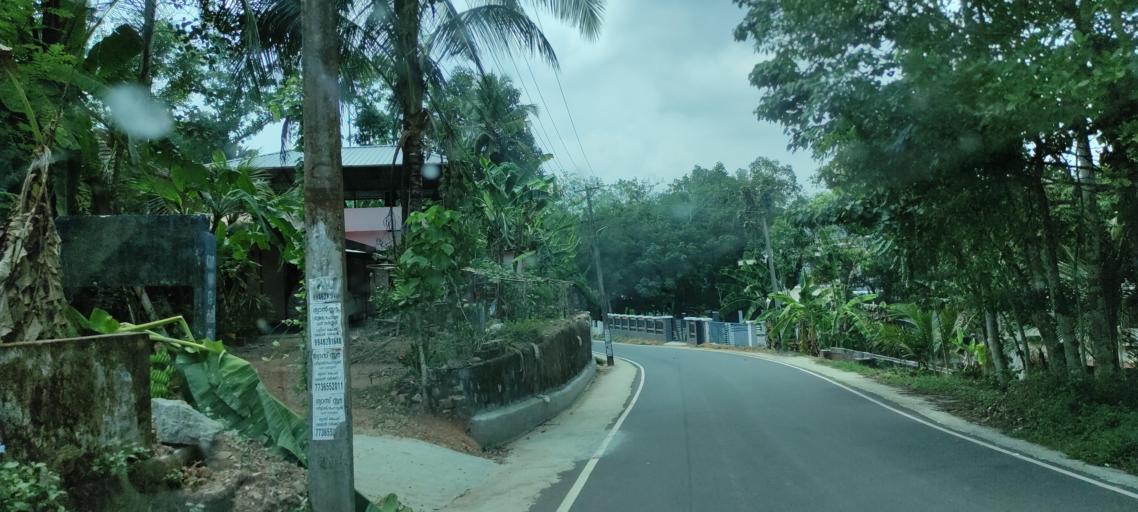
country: IN
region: Kerala
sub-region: Pattanamtitta
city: Adur
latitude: 9.1747
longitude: 76.7480
